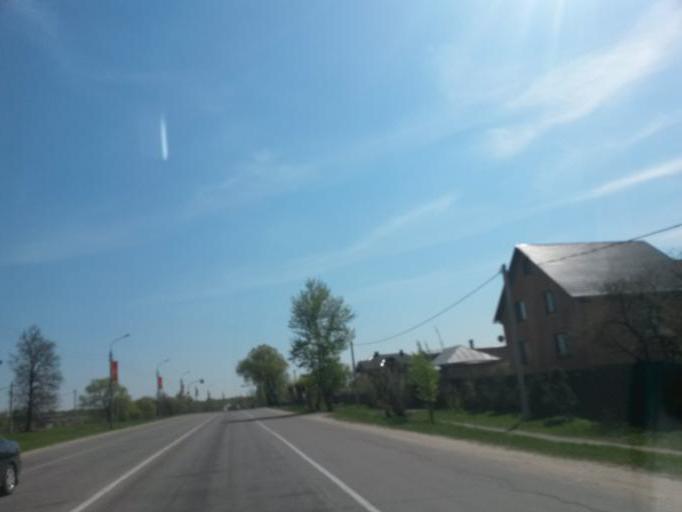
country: RU
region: Moskovskaya
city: Stolbovaya
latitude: 55.2712
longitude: 37.5109
